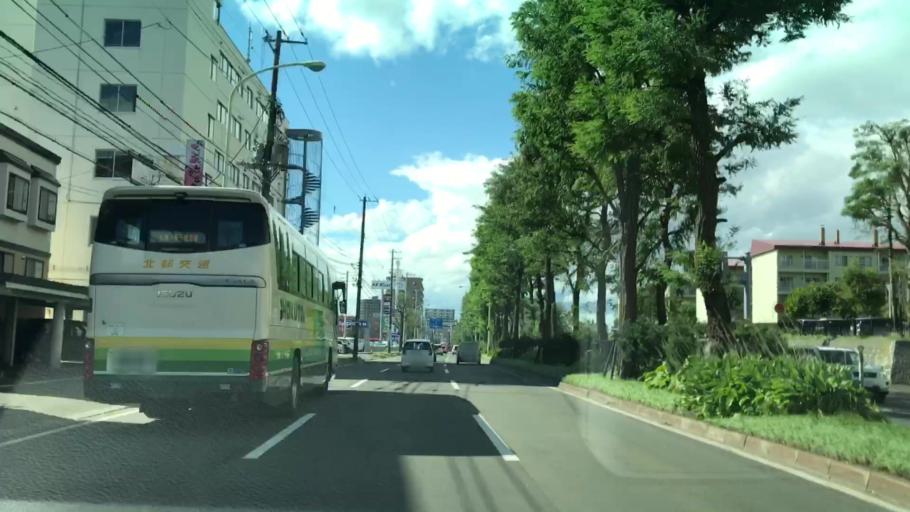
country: JP
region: Hokkaido
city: Sapporo
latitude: 43.0312
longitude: 141.4324
